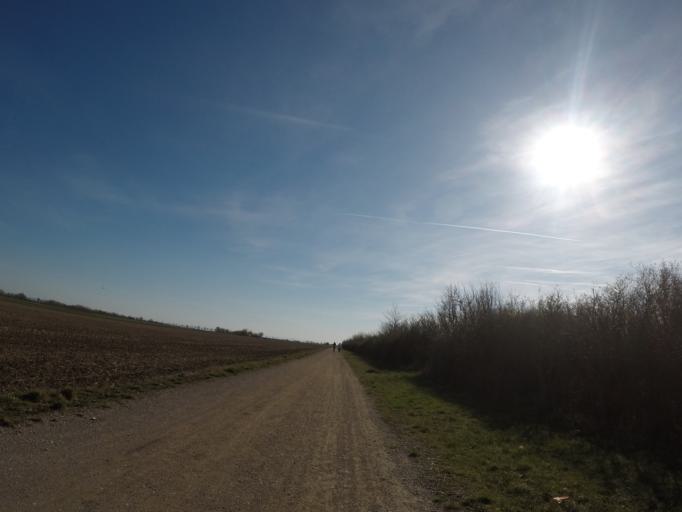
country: AT
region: Lower Austria
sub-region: Politischer Bezirk Modling
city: Vosendorf
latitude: 48.1110
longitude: 16.3398
